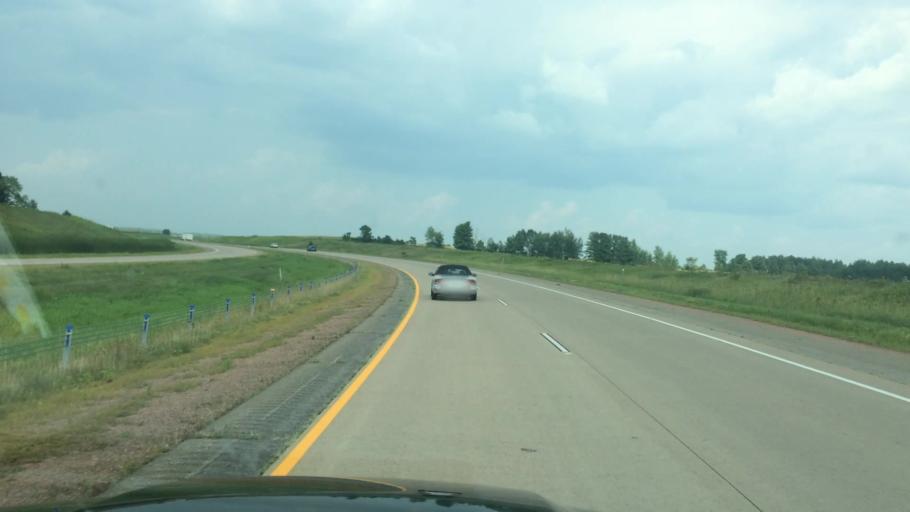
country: US
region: Wisconsin
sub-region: Clark County
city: Abbotsford
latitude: 44.9350
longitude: -90.2946
